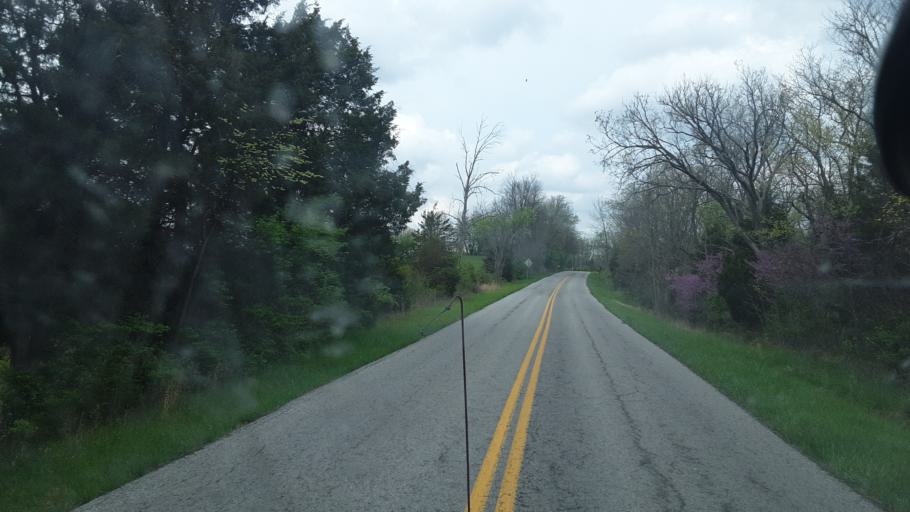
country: US
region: Kentucky
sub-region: Grant County
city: Dry Ridge
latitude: 38.6539
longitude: -84.7027
